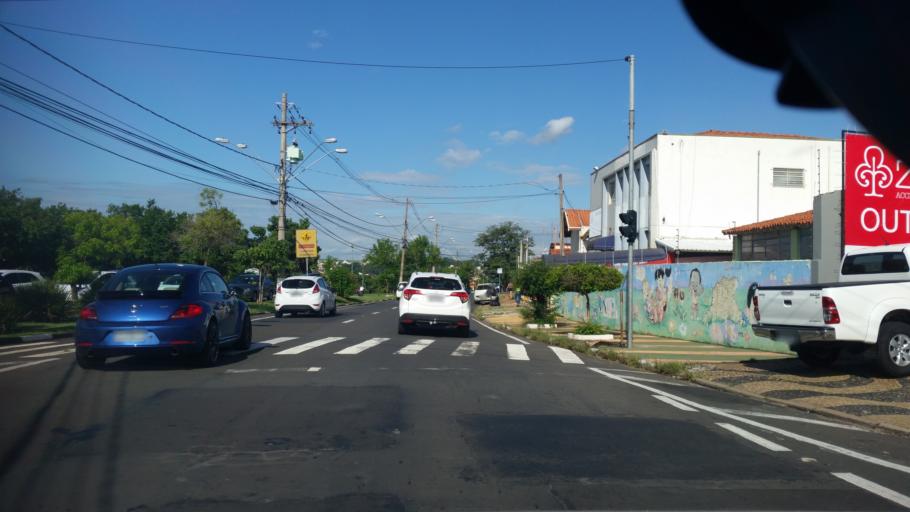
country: BR
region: Sao Paulo
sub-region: Campinas
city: Campinas
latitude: -22.8749
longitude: -47.0447
